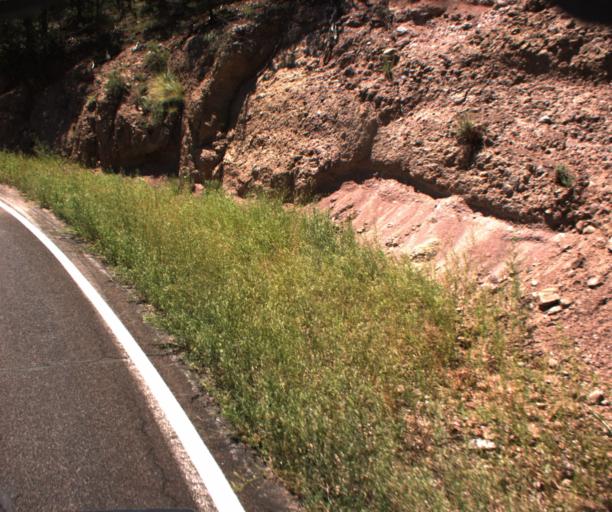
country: US
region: Arizona
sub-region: Greenlee County
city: Morenci
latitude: 33.4096
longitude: -109.3560
